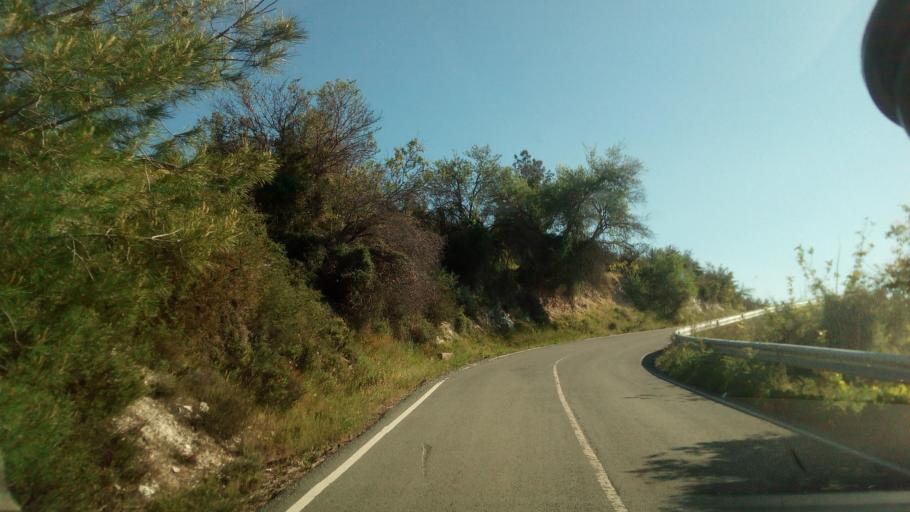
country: CY
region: Limassol
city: Pachna
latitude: 34.8769
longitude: 32.7500
